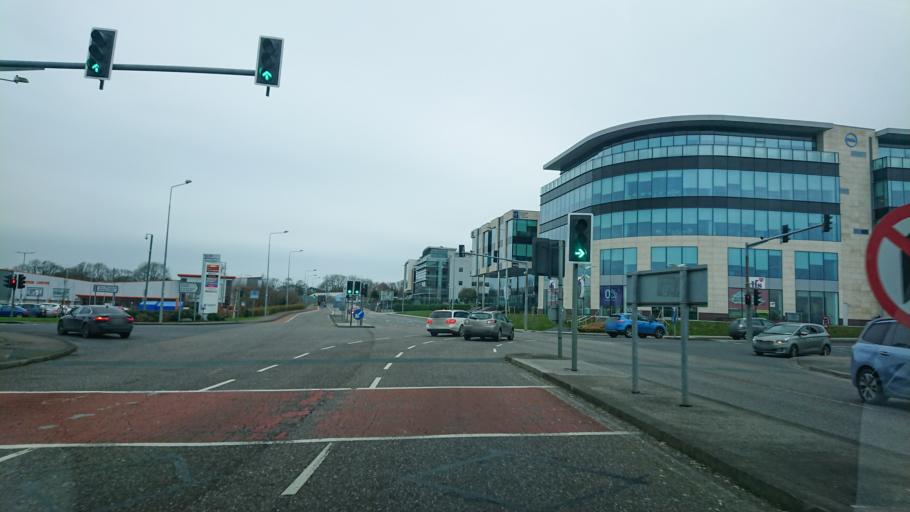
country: IE
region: Munster
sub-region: County Cork
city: Passage West
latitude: 51.8856
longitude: -8.4009
